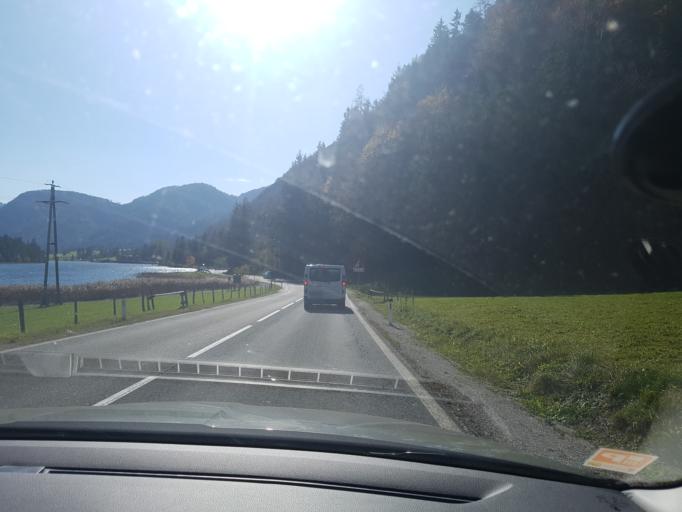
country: AT
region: Tyrol
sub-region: Politischer Bezirk Kitzbuhel
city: Waidring
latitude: 47.5470
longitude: 12.5684
